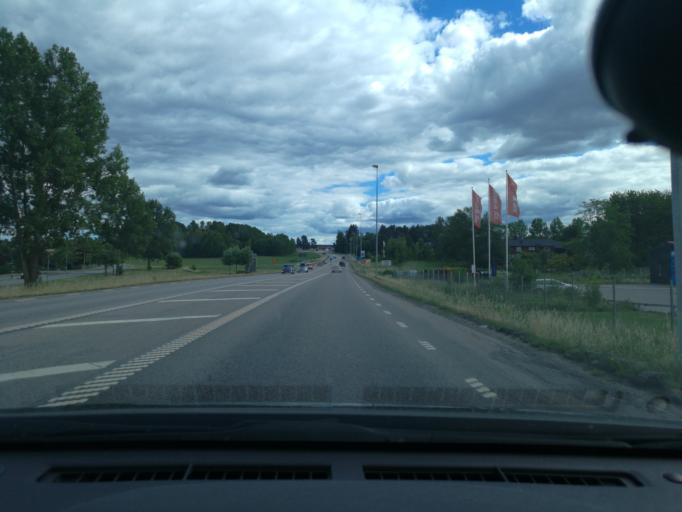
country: SE
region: OEstergoetland
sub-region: Soderkopings Kommun
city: Soederkoeping
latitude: 58.4748
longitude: 16.3367
